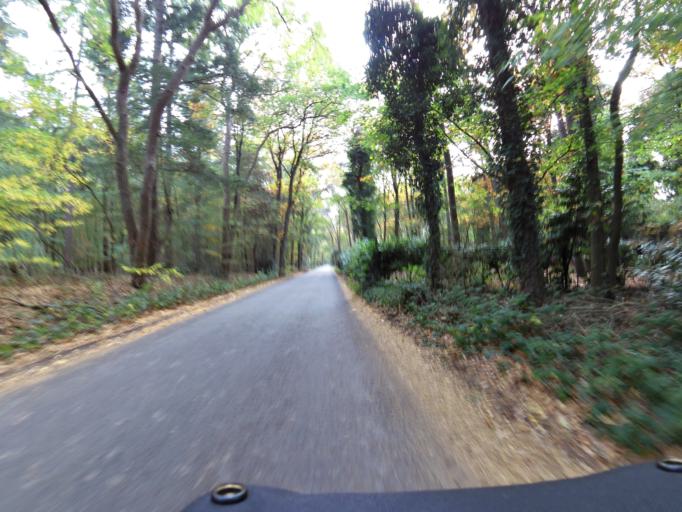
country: NL
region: North Brabant
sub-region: Gemeente Breda
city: Breda
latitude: 51.5449
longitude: 4.7507
